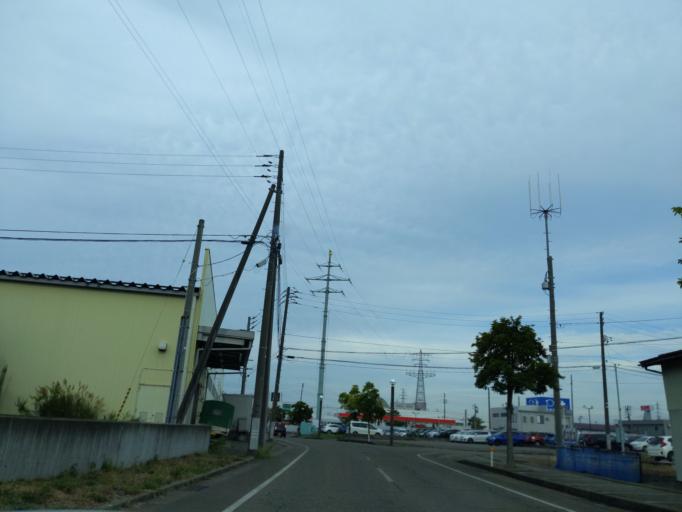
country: JP
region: Niigata
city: Joetsu
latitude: 37.1518
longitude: 138.2540
